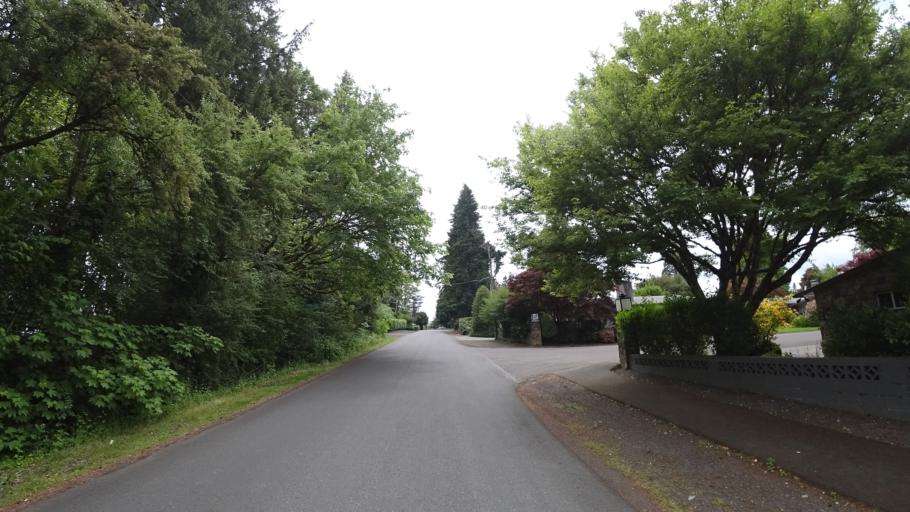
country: US
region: Oregon
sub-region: Washington County
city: Raleigh Hills
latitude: 45.4779
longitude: -122.7641
